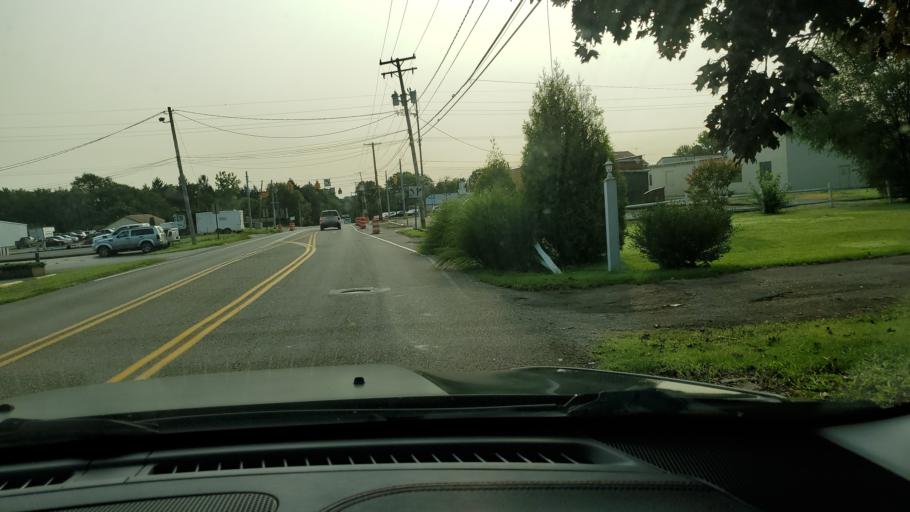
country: US
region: Ohio
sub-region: Mahoning County
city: Poland
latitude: 41.0389
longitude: -80.6362
